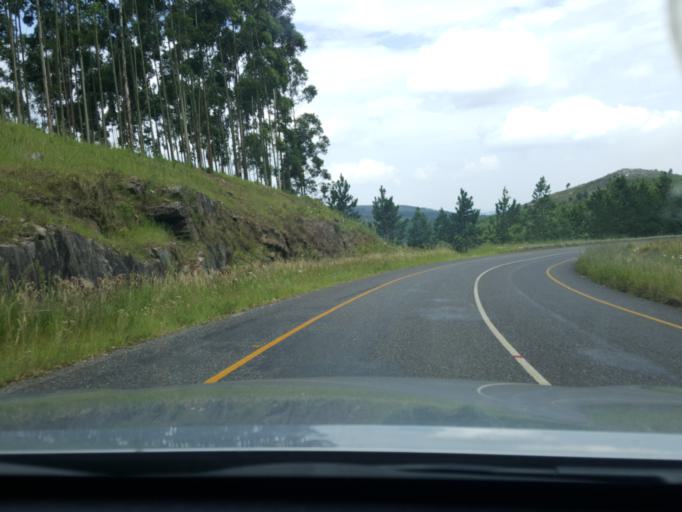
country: ZA
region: Mpumalanga
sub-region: Ehlanzeni District
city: White River
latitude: -25.1683
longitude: 30.8676
